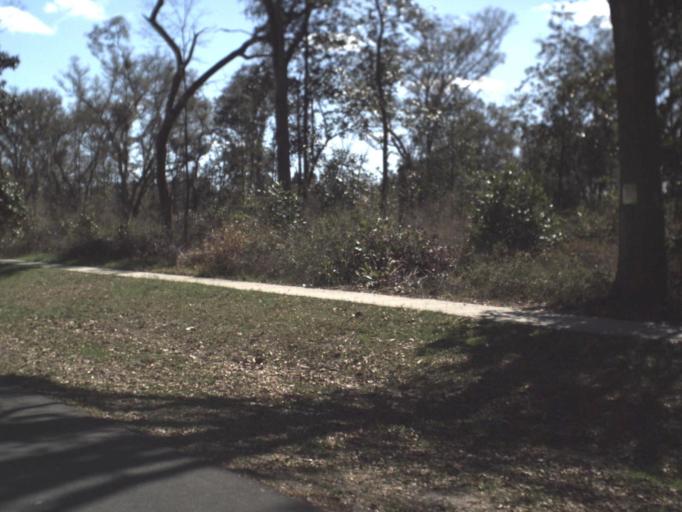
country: US
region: Florida
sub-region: Gadsden County
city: Gretna
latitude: 30.6089
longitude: -84.6578
